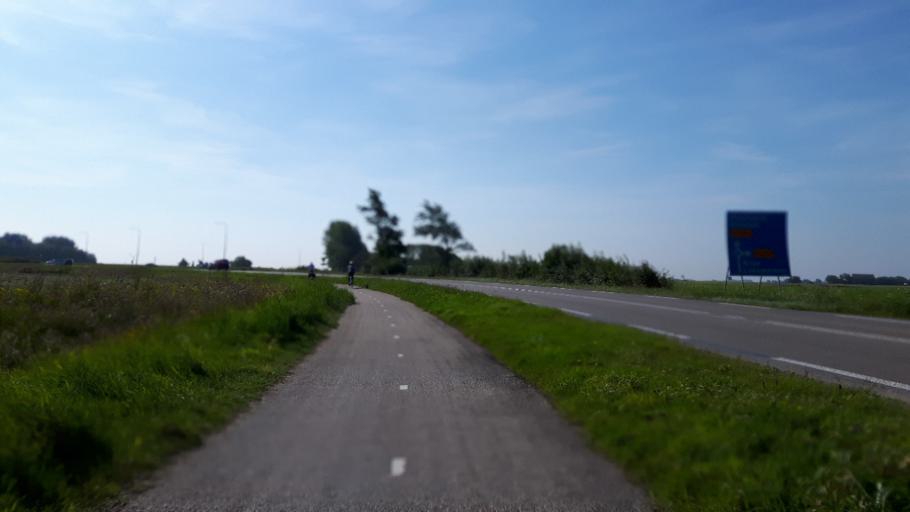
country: NL
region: Friesland
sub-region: Gemeente Dongeradeel
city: Holwerd
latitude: 53.3702
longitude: 5.8945
